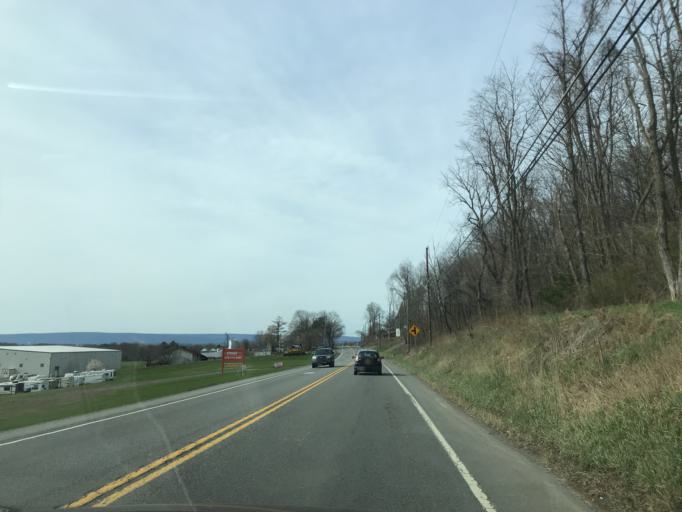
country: US
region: Pennsylvania
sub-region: Union County
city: Lewisburg
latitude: 40.9262
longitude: -76.8460
